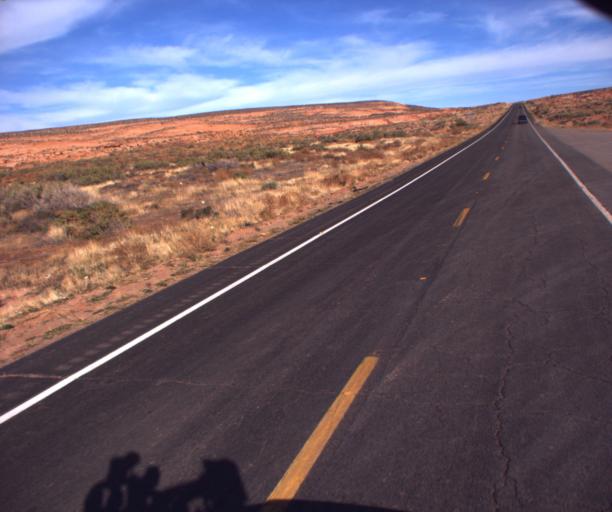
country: US
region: Arizona
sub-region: Apache County
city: Many Farms
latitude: 36.9243
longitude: -109.6031
